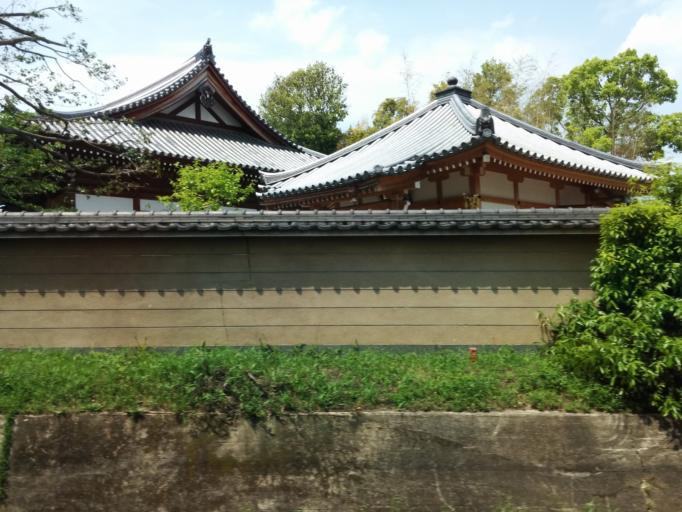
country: JP
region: Osaka
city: Ibaraki
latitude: 34.8003
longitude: 135.5636
